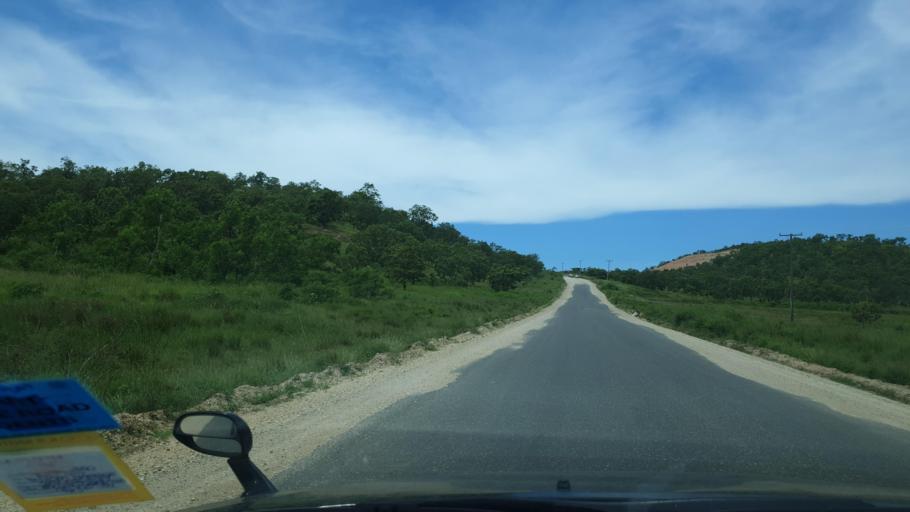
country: PG
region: National Capital
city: Port Moresby
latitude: -9.4327
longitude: 147.0742
